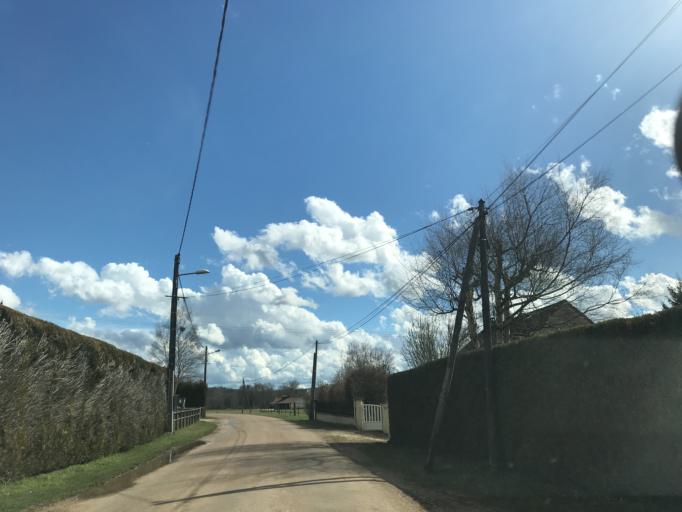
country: FR
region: Bourgogne
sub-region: Departement de l'Yonne
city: Fontenailles
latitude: 47.5122
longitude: 3.5000
